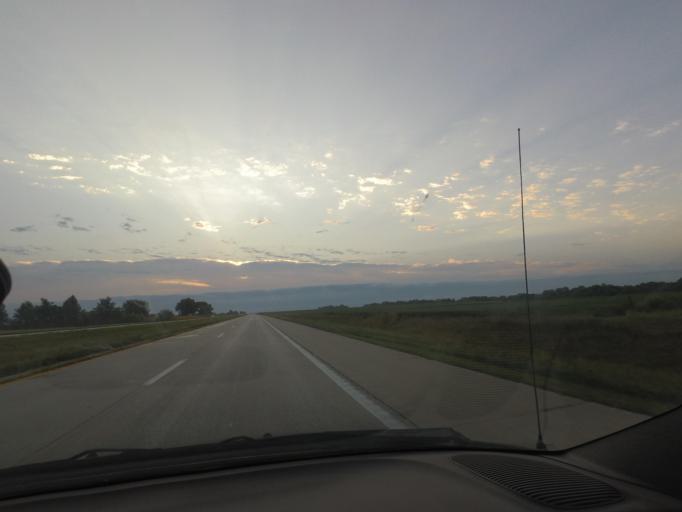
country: US
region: Missouri
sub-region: Macon County
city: Macon
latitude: 39.7502
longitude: -92.3526
